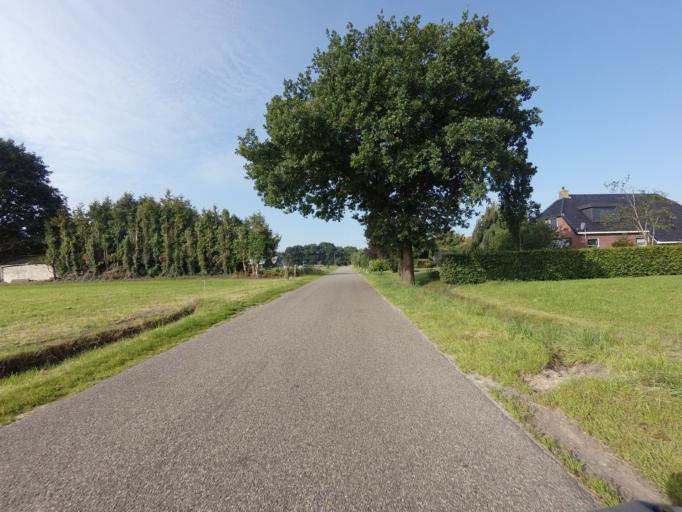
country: NL
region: Friesland
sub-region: Gemeente Weststellingwerf
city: Noordwolde
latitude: 52.9223
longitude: 6.1702
